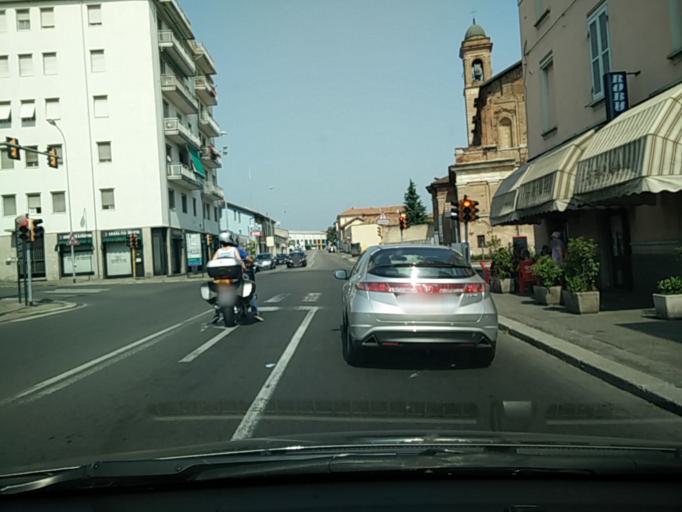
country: IT
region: Lombardy
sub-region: Provincia di Pavia
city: Pavia
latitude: 45.1818
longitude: 9.1705
